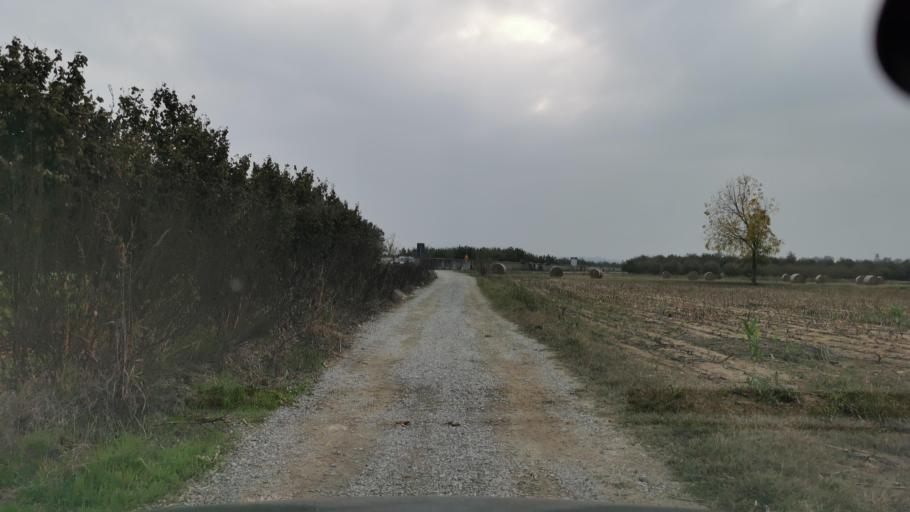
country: IT
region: Piedmont
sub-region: Provincia di Cuneo
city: Cinzano
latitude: 44.6861
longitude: 7.9122
